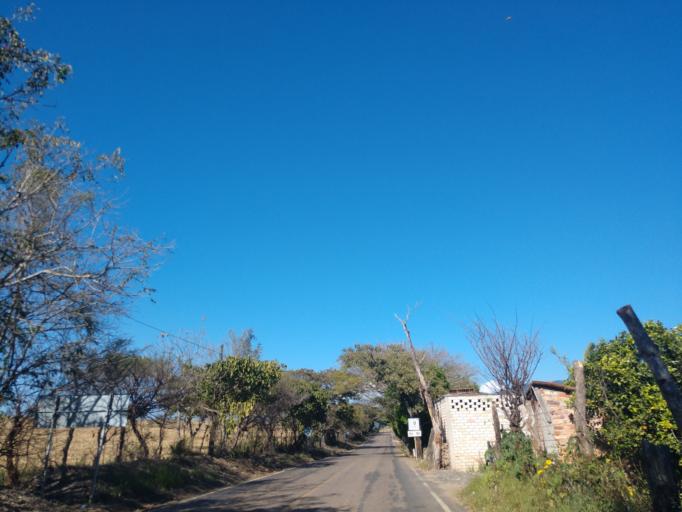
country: MX
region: Nayarit
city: Compostela
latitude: 21.2562
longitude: -104.8994
